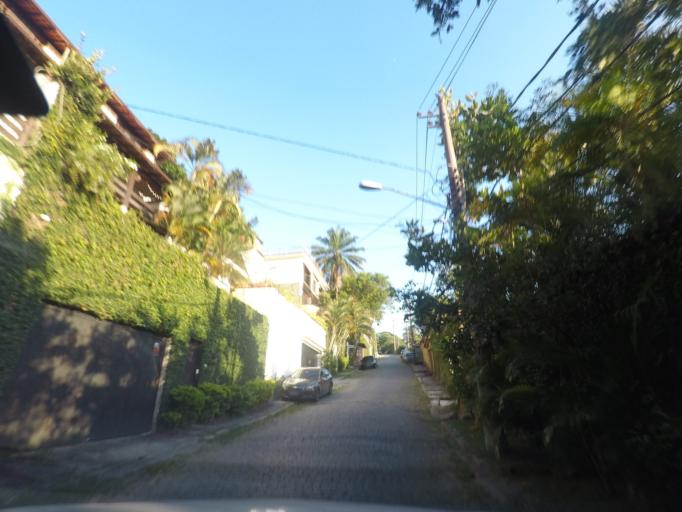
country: BR
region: Rio de Janeiro
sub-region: Rio De Janeiro
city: Rio de Janeiro
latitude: -22.9424
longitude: -43.1937
